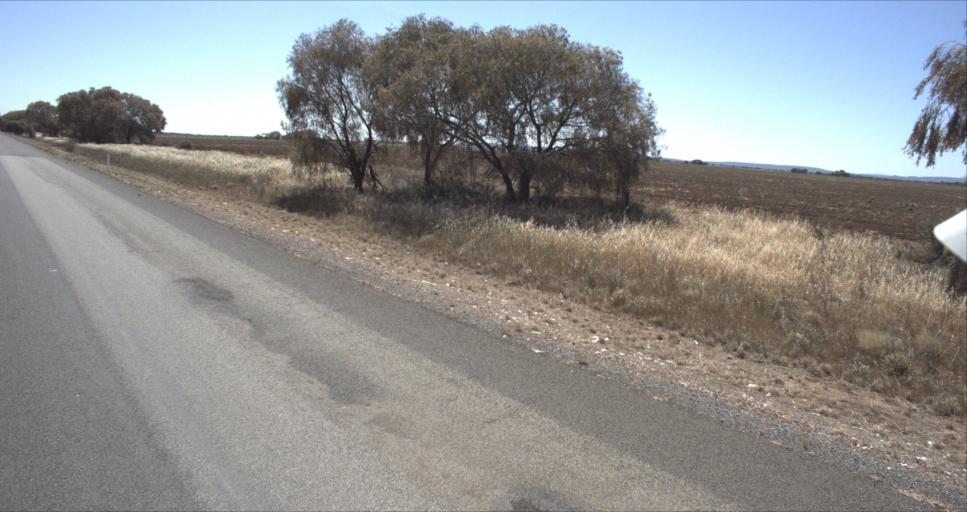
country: AU
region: New South Wales
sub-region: Leeton
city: Leeton
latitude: -34.4785
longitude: 146.2910
